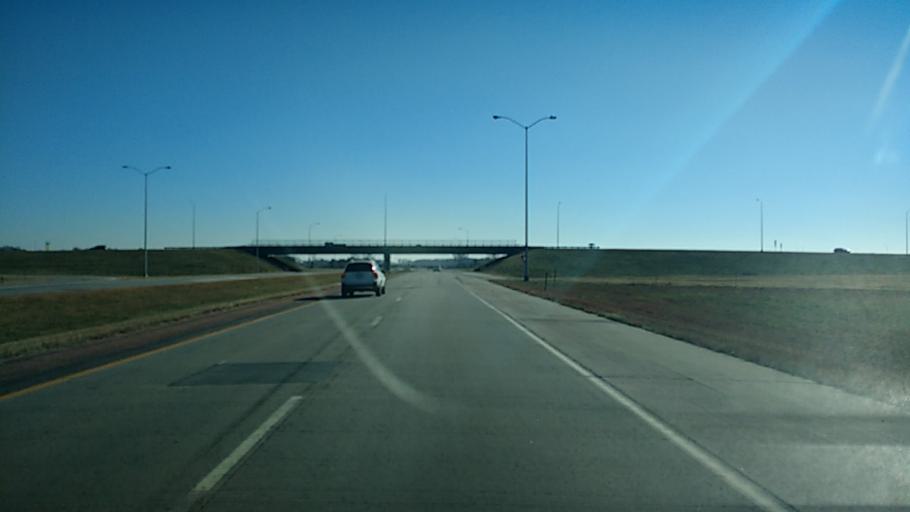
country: US
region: South Dakota
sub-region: Union County
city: Dakota Dunes
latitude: 42.5066
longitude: -96.4915
